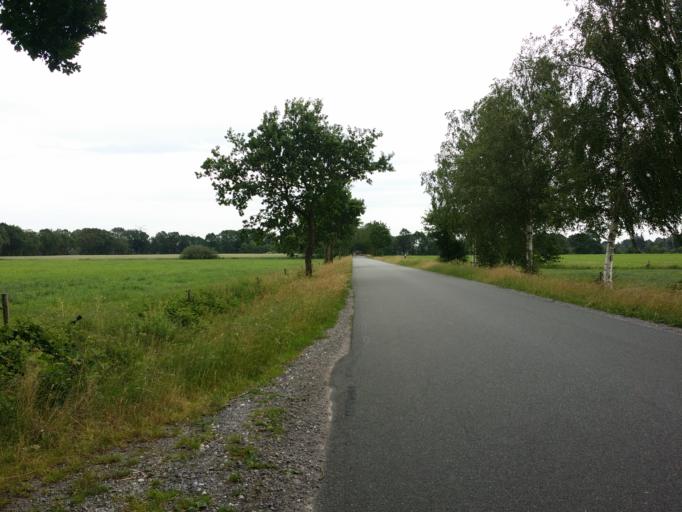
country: DE
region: Lower Saxony
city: Bockhorn
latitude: 53.3516
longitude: 8.0199
